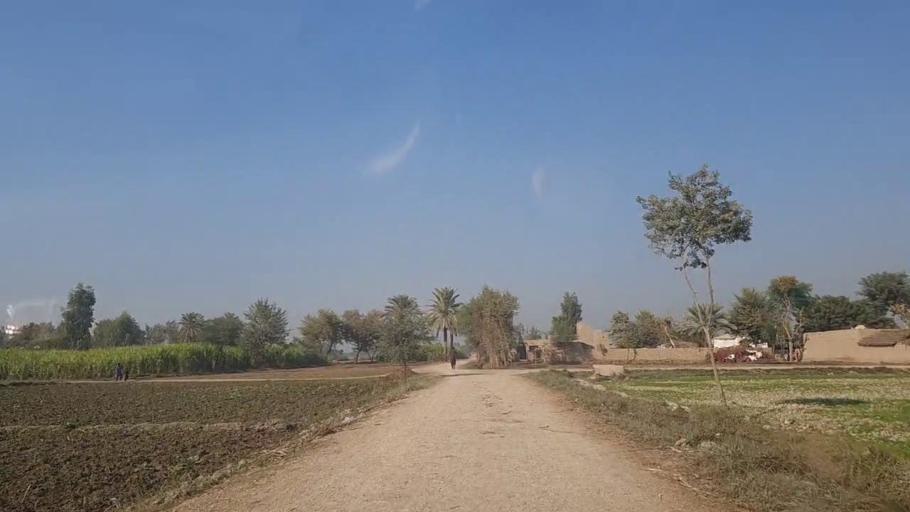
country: PK
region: Sindh
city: Gambat
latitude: 27.3704
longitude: 68.4746
